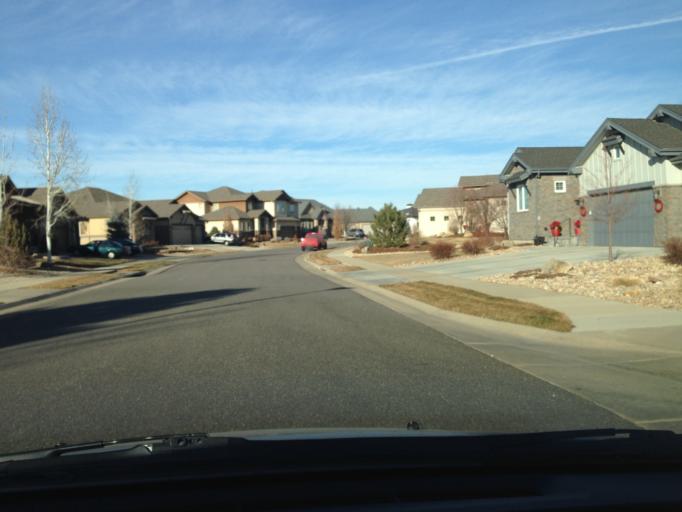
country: US
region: Colorado
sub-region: Boulder County
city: Erie
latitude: 40.0419
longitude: -105.0828
